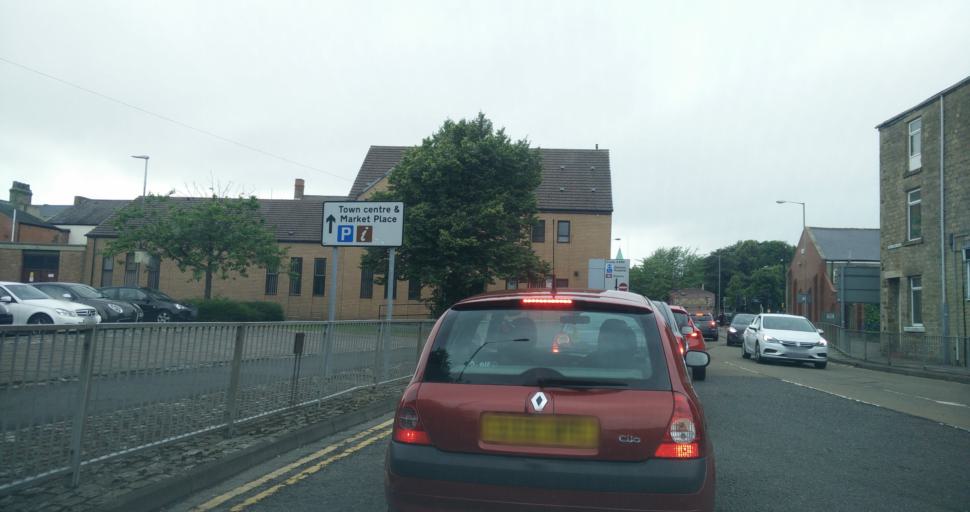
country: GB
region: England
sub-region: County Durham
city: Bishop Auckland
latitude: 54.6614
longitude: -1.6742
